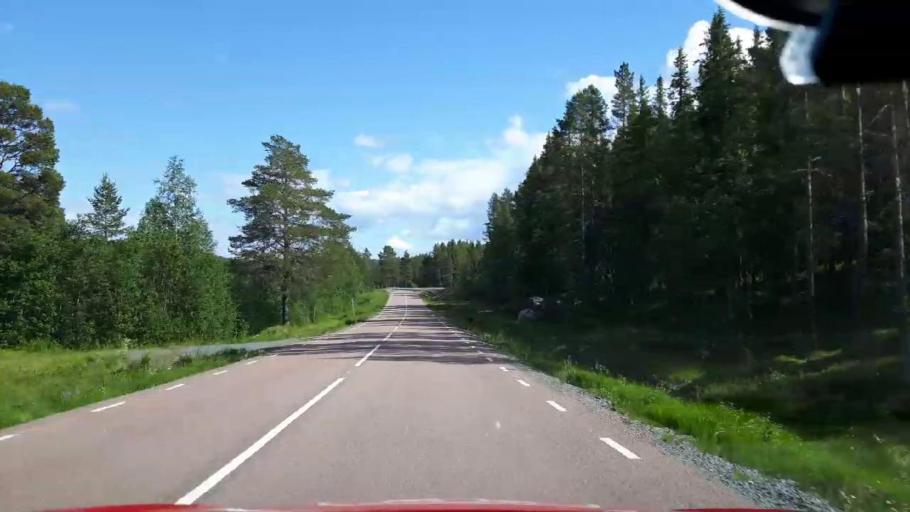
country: SE
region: Jaemtland
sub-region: Krokoms Kommun
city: Valla
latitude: 64.0116
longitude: 14.2282
